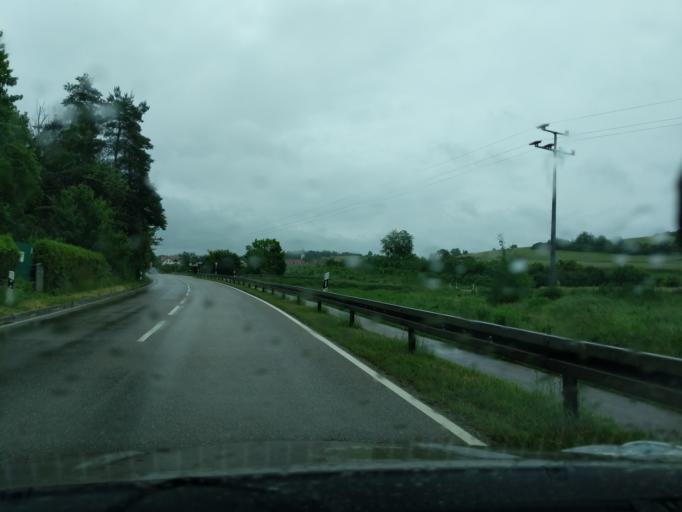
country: DE
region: Bavaria
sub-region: Upper Palatinate
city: Sinzing
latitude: 49.0330
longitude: 12.0321
